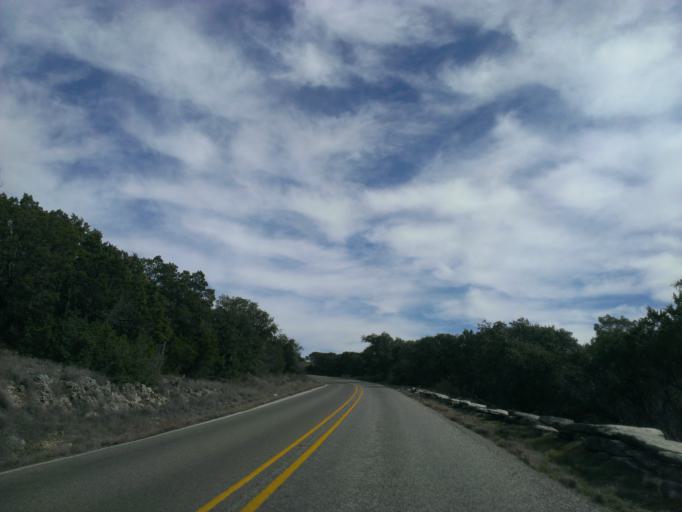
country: US
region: Texas
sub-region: Llano County
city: Buchanan Dam
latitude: 30.6962
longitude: -98.3770
